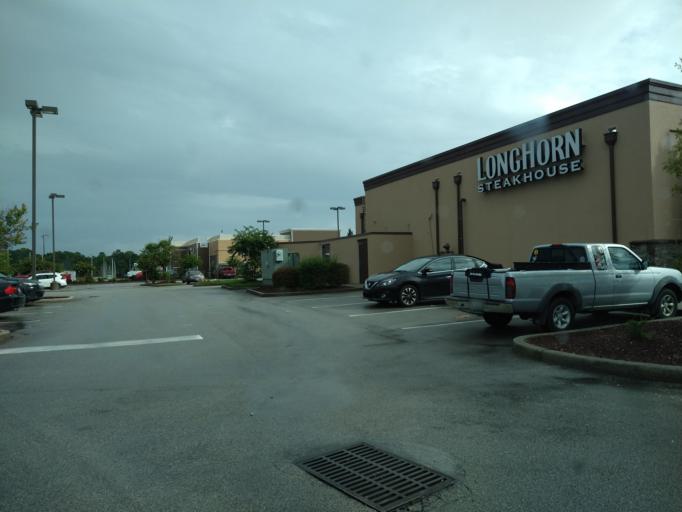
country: US
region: North Carolina
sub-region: Onslow County
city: Pumpkin Center
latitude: 34.7967
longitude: -77.4103
